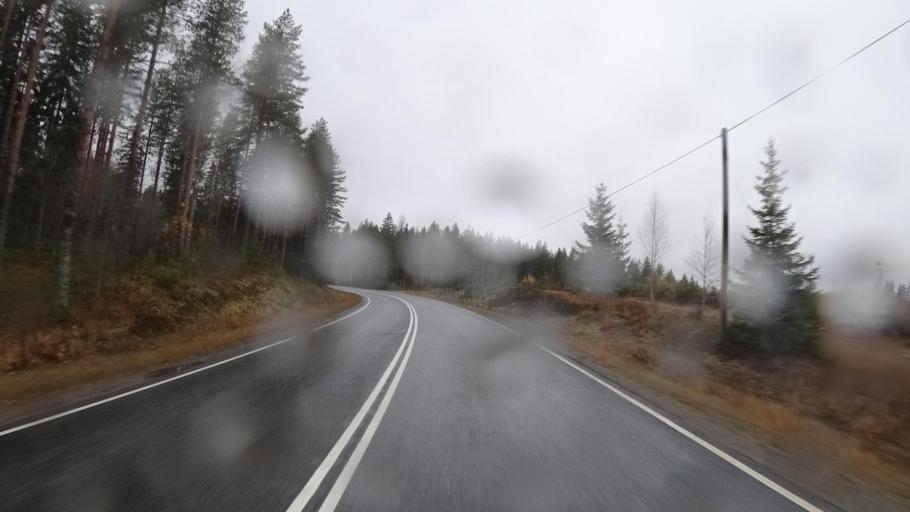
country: FI
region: Northern Savo
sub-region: Koillis-Savo
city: Tuusniemi
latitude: 62.8711
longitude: 28.3845
